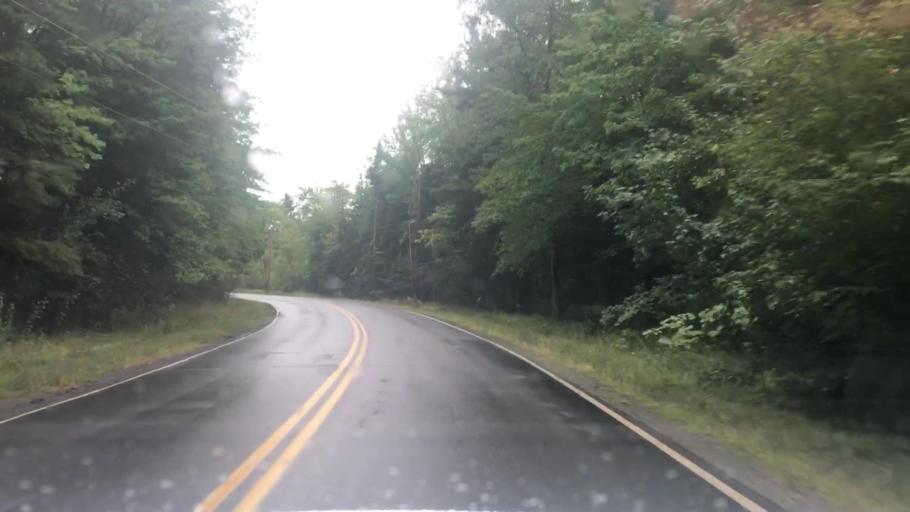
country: US
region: Maine
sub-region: Penobscot County
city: Hudson
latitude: 44.9871
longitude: -68.7967
